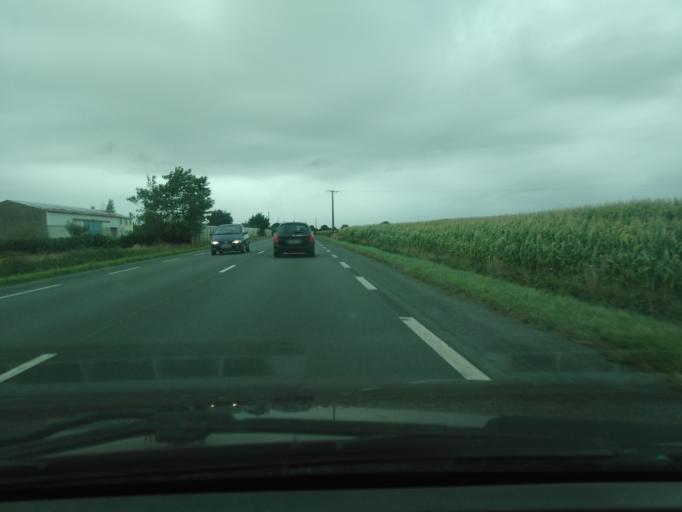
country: FR
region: Pays de la Loire
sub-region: Departement de la Vendee
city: Sainte-Gemme-la-Plaine
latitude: 46.4570
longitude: -1.1056
